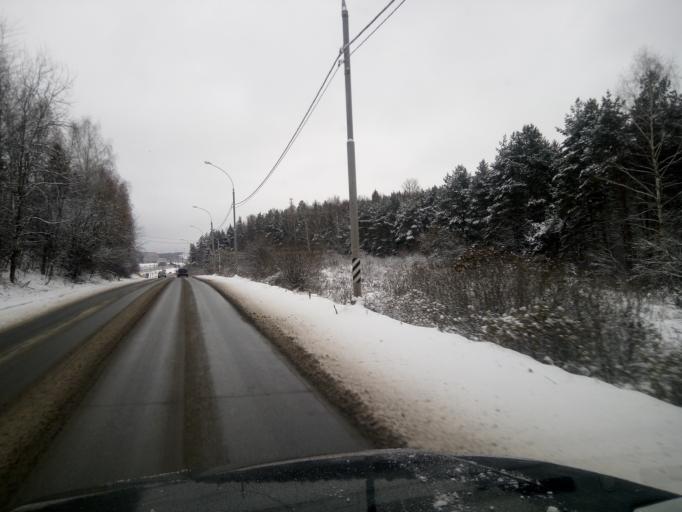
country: RU
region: Moskovskaya
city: Skhodnya
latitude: 55.9655
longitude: 37.3098
